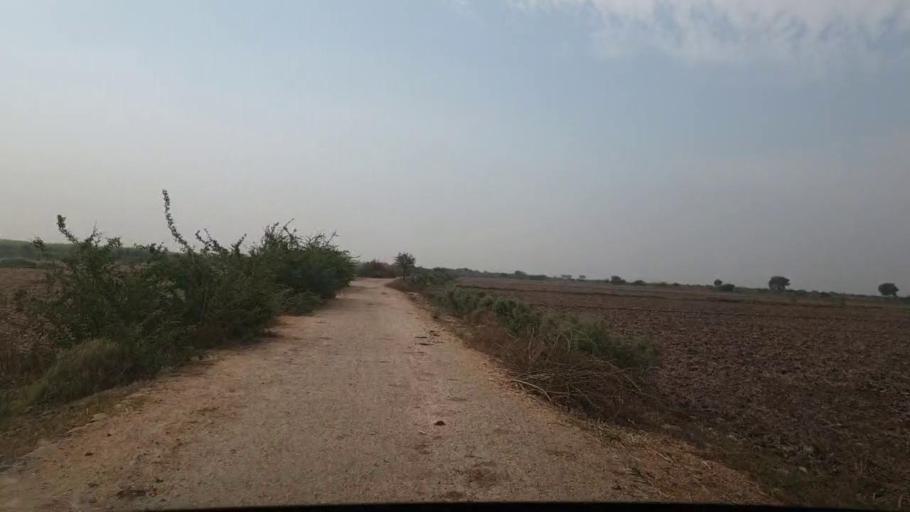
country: PK
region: Sindh
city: Chuhar Jamali
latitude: 24.4100
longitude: 67.9382
